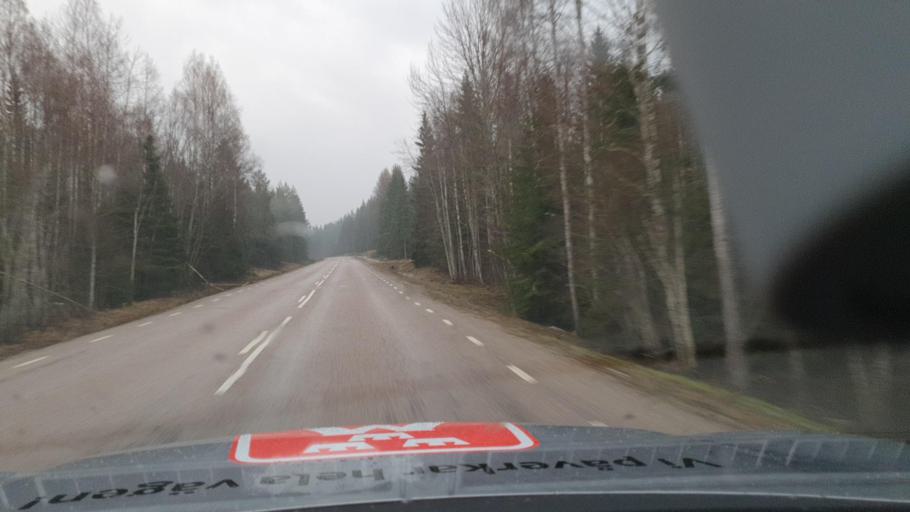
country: SE
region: Vaesternorrland
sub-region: OErnskoeldsviks Kommun
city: Bjasta
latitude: 63.2322
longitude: 18.4467
